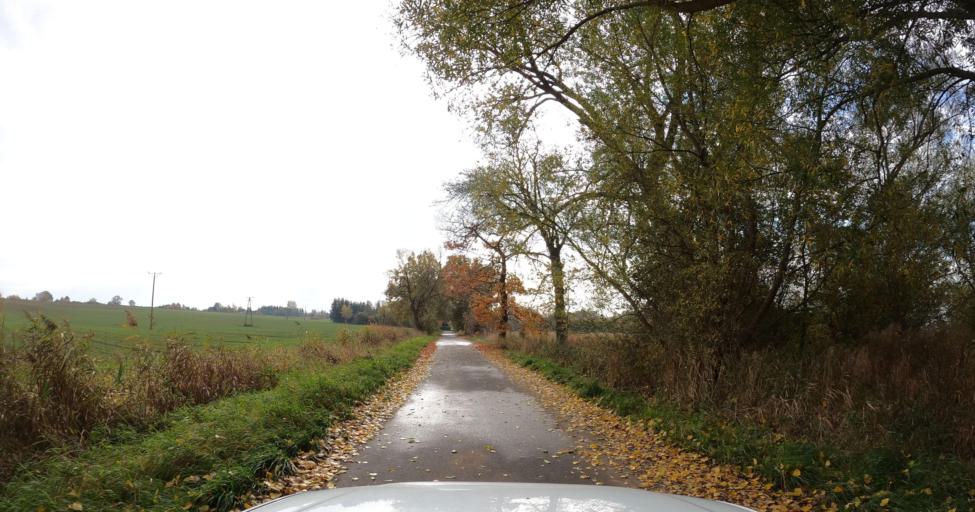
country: PL
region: West Pomeranian Voivodeship
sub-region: Powiat kamienski
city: Kamien Pomorski
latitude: 53.9798
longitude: 14.8481
